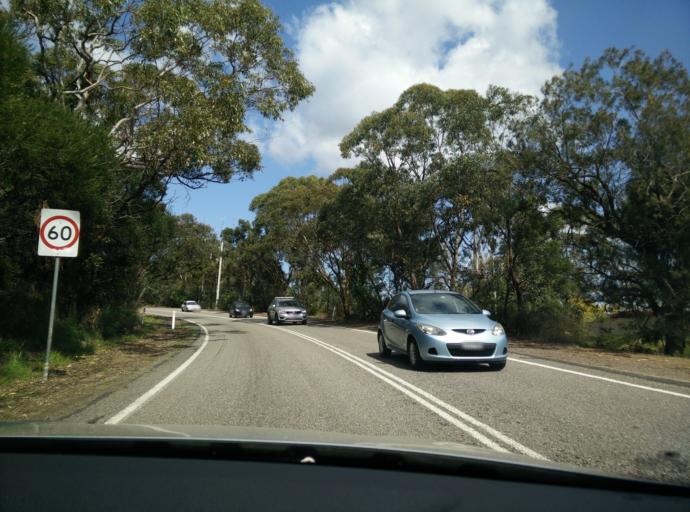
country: AU
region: New South Wales
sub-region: Gosford Shire
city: Point Clare
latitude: -33.4432
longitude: 151.2937
